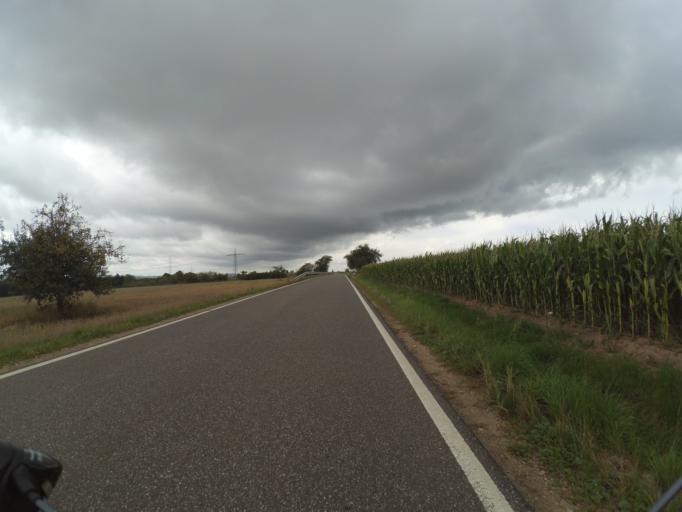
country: DE
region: Rheinland-Pfalz
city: Orenhofen
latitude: 49.8985
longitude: 6.6745
